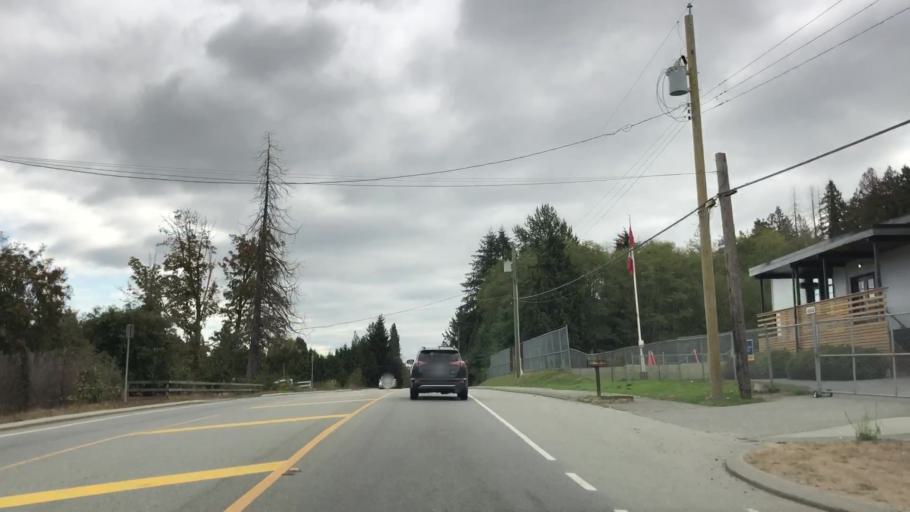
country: CA
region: British Columbia
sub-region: Greater Vancouver Regional District
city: White Rock
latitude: 49.0603
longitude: -122.7556
